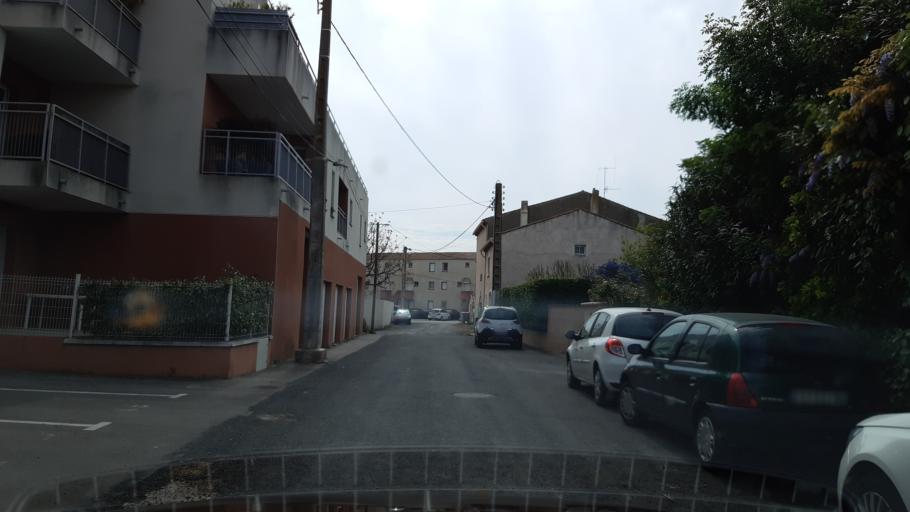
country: FR
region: Languedoc-Roussillon
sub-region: Departement de l'Aude
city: Narbonne
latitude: 43.1904
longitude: 2.9958
